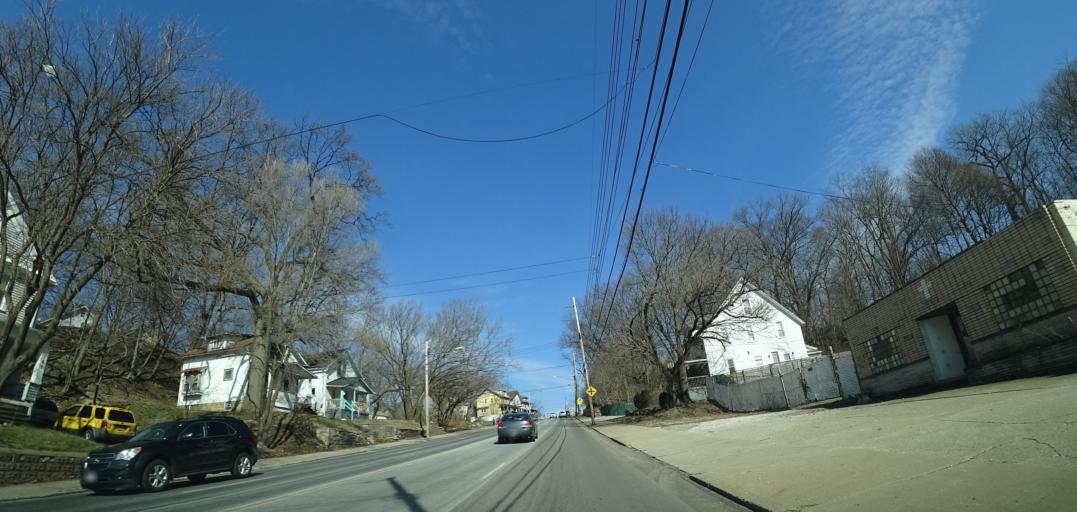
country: US
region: Ohio
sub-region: Summit County
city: Akron
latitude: 41.1017
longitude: -81.5214
